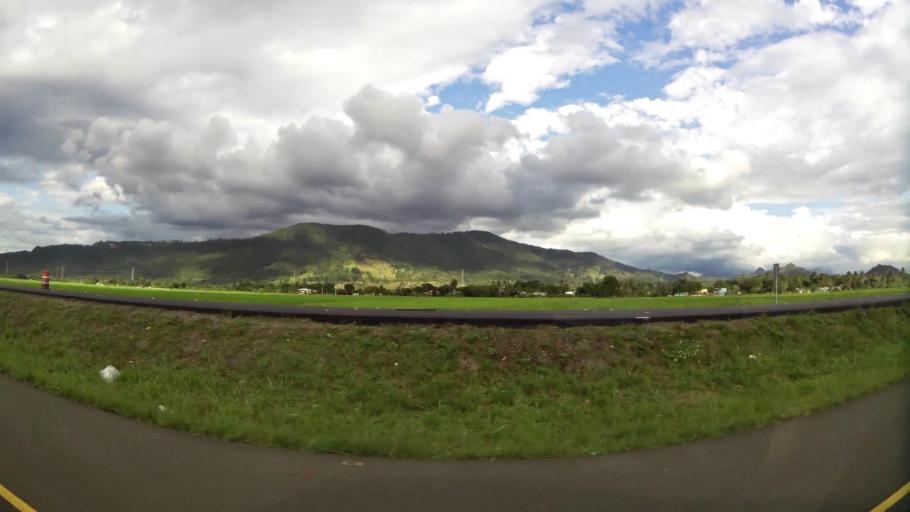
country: DO
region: Monsenor Nouel
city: Bonao
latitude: 18.8905
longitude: -70.3676
